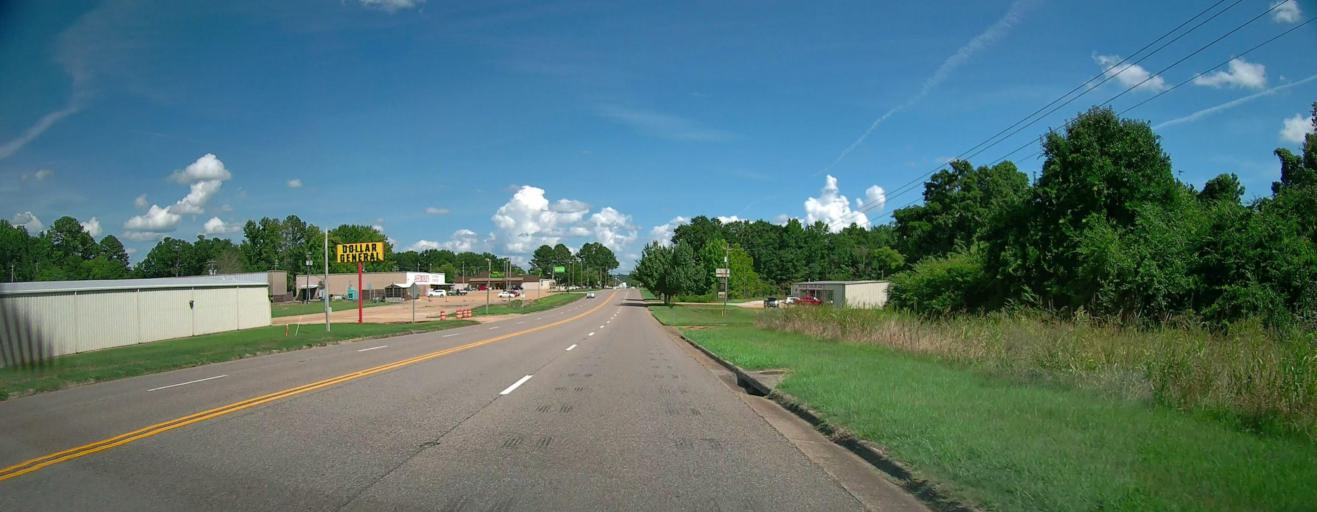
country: US
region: Alabama
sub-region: Pickens County
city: Reform
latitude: 33.3842
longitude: -88.0268
